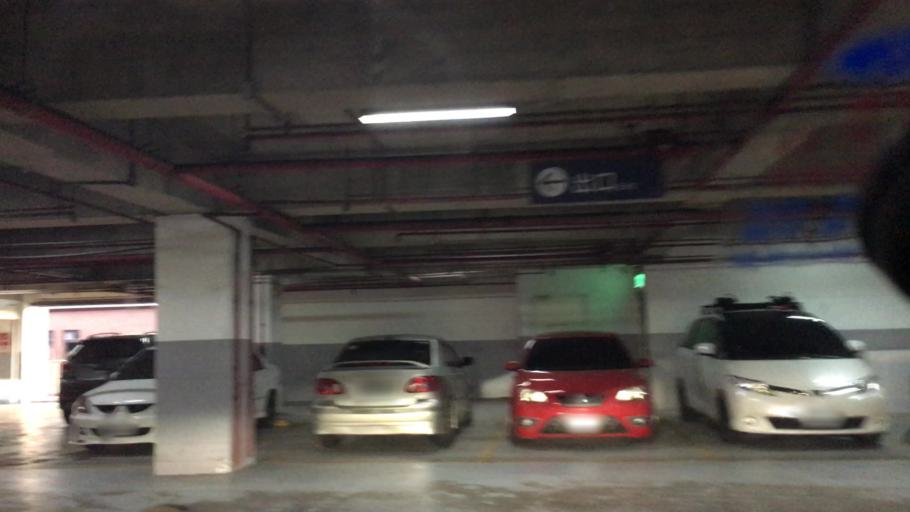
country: TW
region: Taiwan
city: Taoyuan City
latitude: 24.9891
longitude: 121.2866
